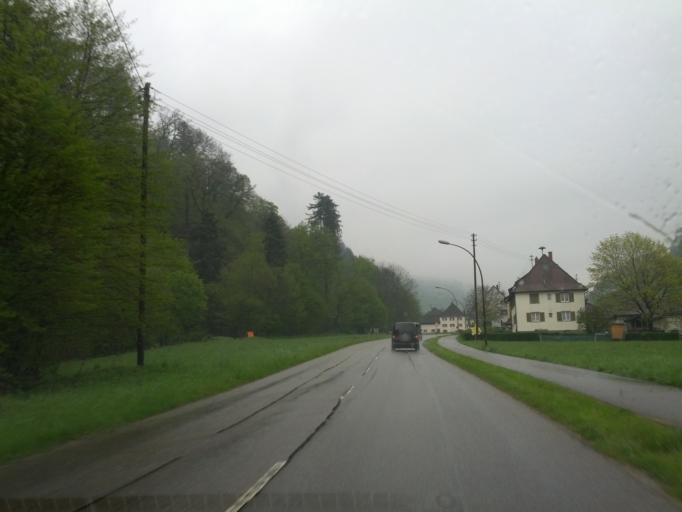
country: DE
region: Baden-Wuerttemberg
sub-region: Freiburg Region
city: Muenstertal/Schwarzwald
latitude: 47.8663
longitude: 7.8041
